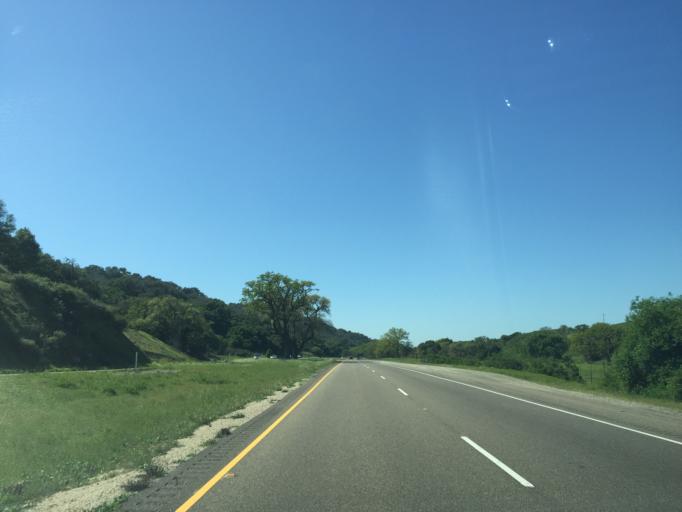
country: US
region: California
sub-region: Santa Barbara County
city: Los Alamos
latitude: 34.7176
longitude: -120.1979
